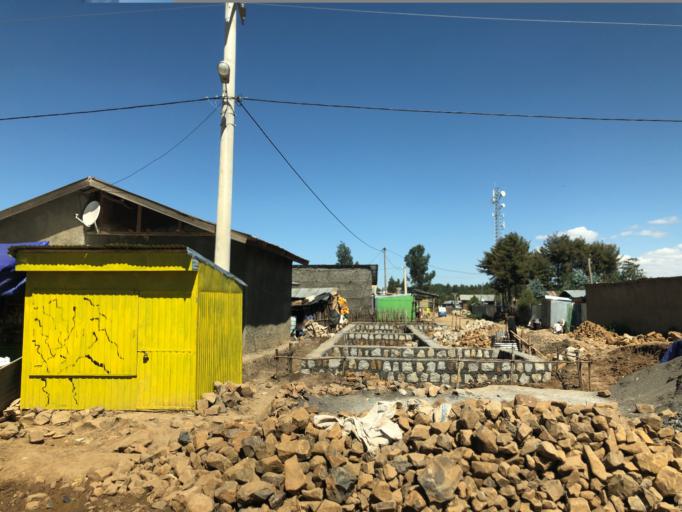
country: ET
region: Amhara
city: Lalibela
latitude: 11.6890
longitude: 38.9234
